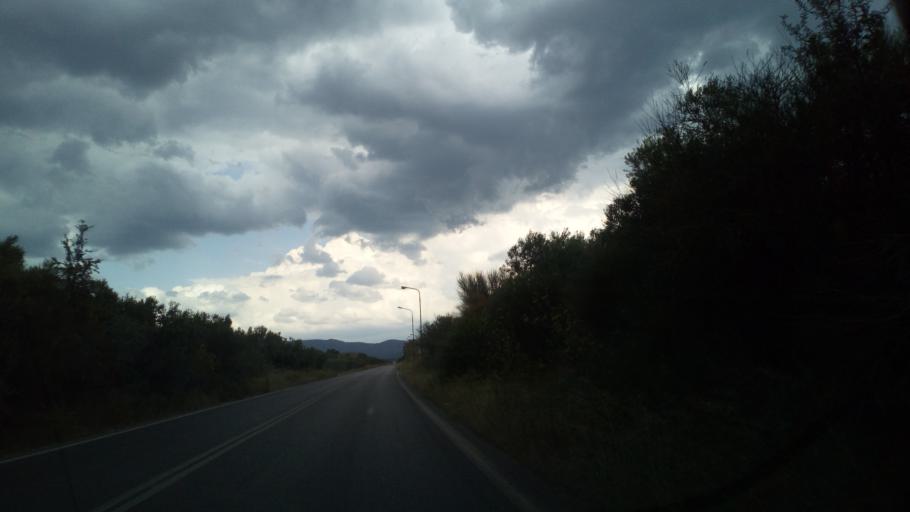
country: GR
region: Central Macedonia
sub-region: Nomos Chalkidikis
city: Kalyves Polygyrou
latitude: 40.3001
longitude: 23.4328
